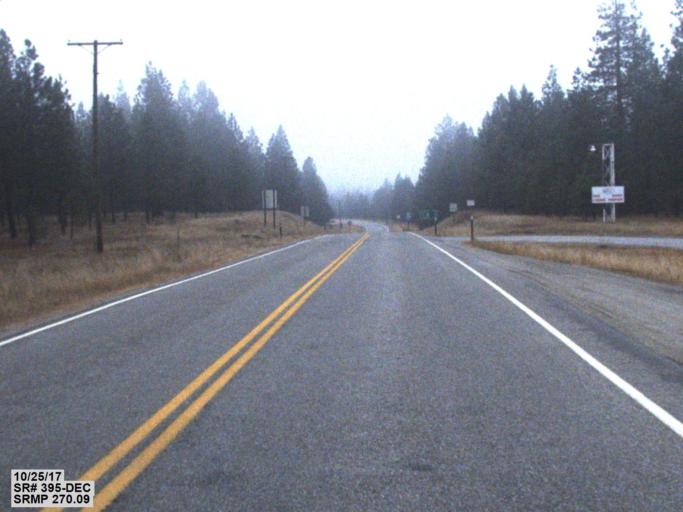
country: CA
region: British Columbia
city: Grand Forks
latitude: 48.9977
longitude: -118.2245
